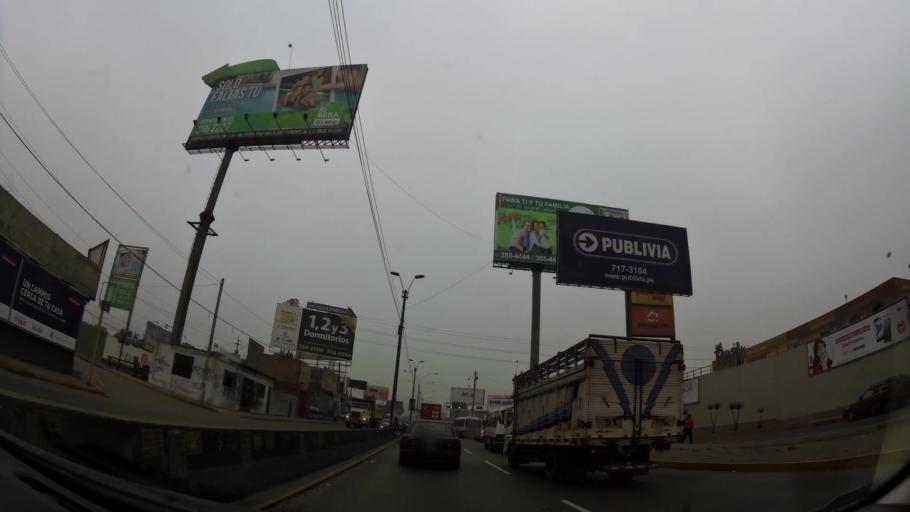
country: PE
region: Lima
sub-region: Lima
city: Santa Maria
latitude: -12.0148
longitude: -76.8859
